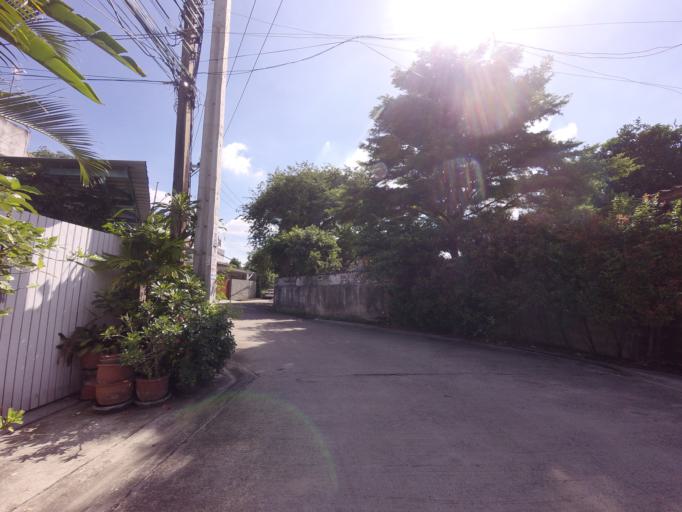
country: TH
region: Bangkok
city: Lat Phrao
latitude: 13.7943
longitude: 100.5904
